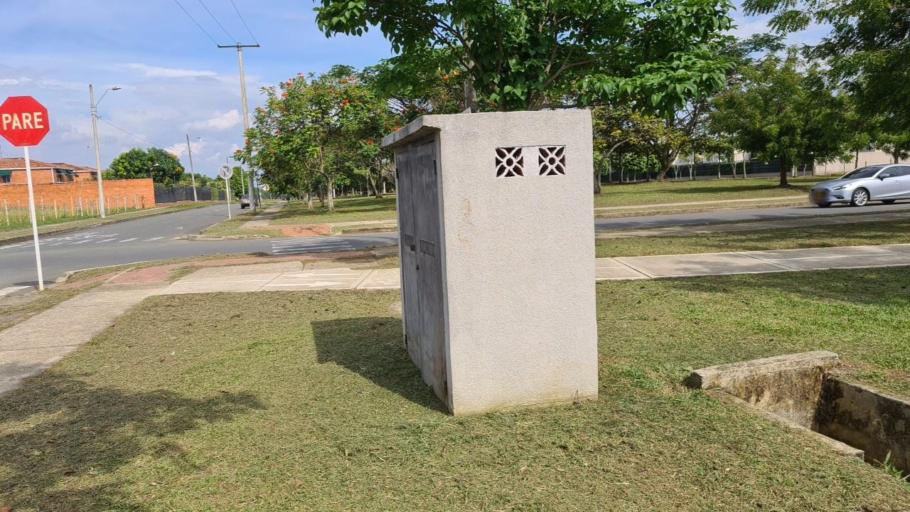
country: CO
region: Valle del Cauca
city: Jamundi
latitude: 3.2559
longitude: -76.5640
